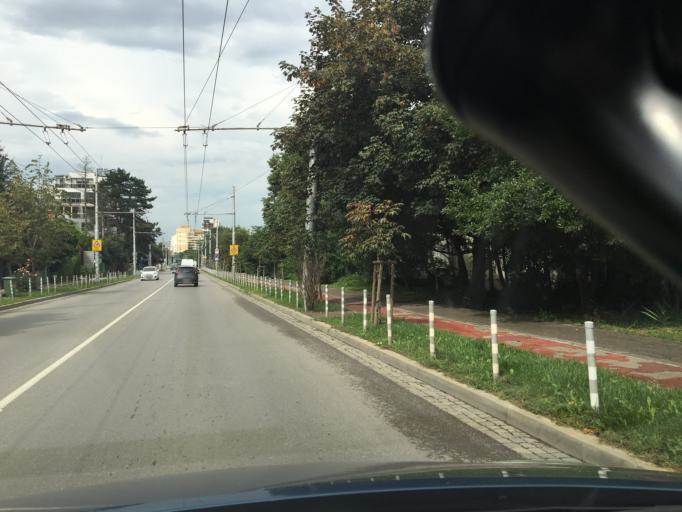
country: BG
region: Sofia-Capital
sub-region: Stolichna Obshtina
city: Sofia
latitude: 42.6635
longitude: 23.2745
